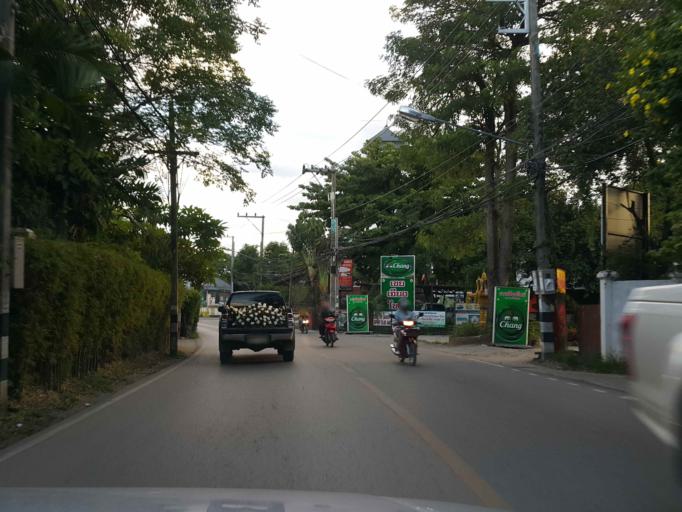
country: TH
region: Chiang Mai
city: Chiang Mai
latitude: 18.8009
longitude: 99.0050
